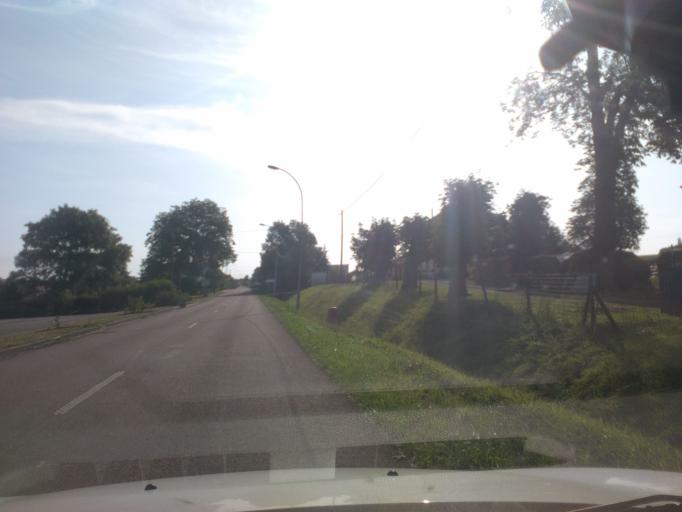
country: FR
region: Lorraine
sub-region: Departement des Vosges
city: Mirecourt
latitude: 48.3086
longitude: 6.0441
